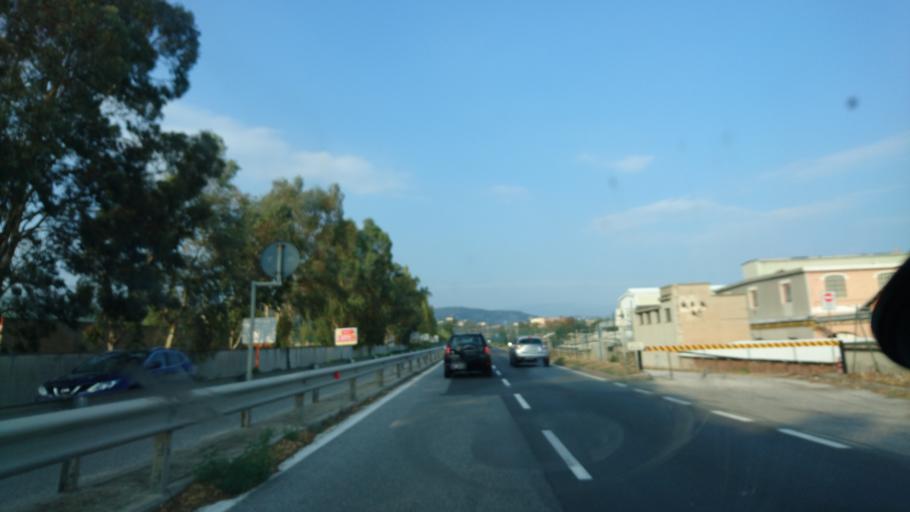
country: IT
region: Liguria
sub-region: Provincia di Savona
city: Valleggia
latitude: 44.2769
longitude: 8.4360
